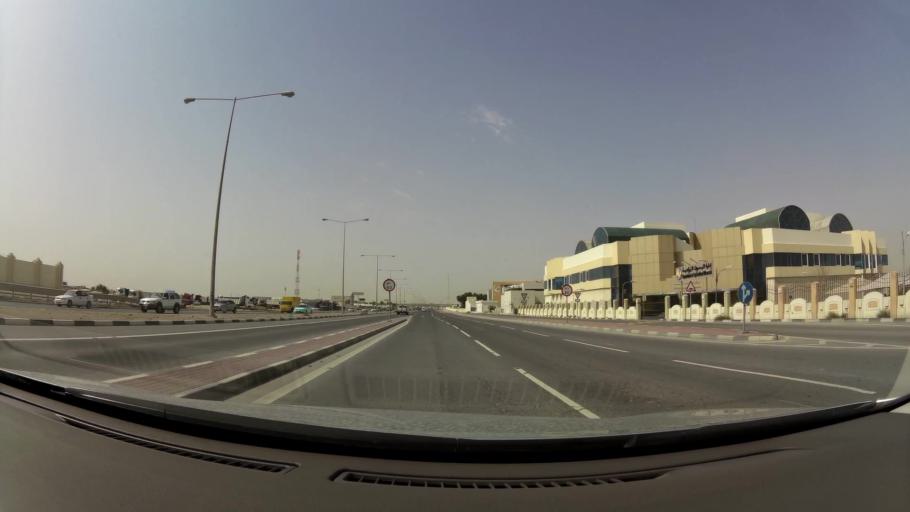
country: QA
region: Baladiyat ad Dawhah
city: Doha
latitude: 25.2359
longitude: 51.5209
